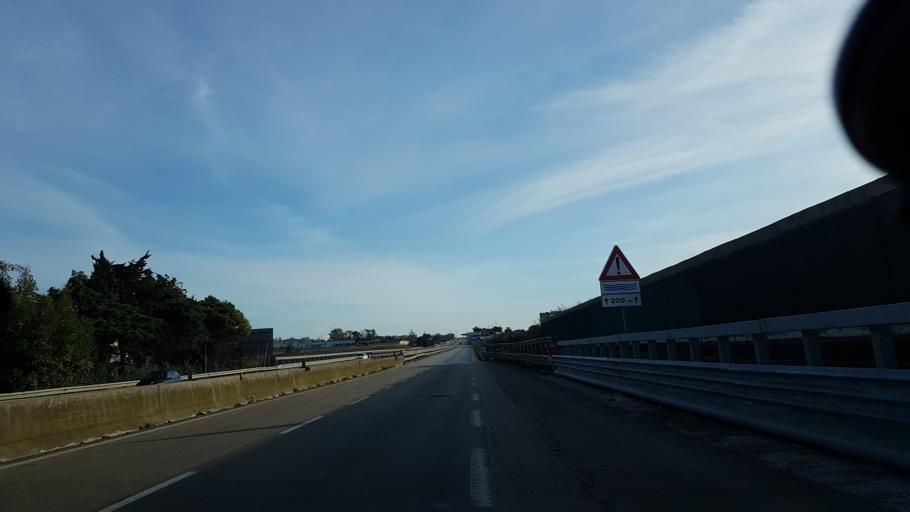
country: IT
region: Apulia
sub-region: Provincia di Brindisi
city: Brindisi
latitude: 40.6402
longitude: 17.9149
